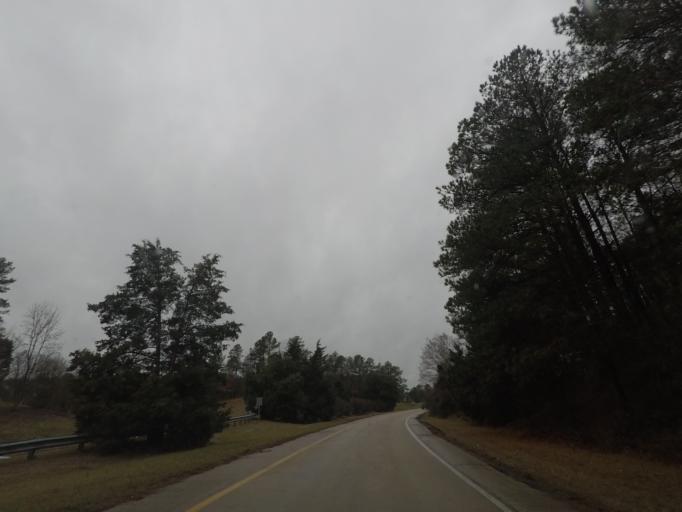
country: US
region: North Carolina
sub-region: Wake County
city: Morrisville
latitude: 35.9024
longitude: -78.8756
